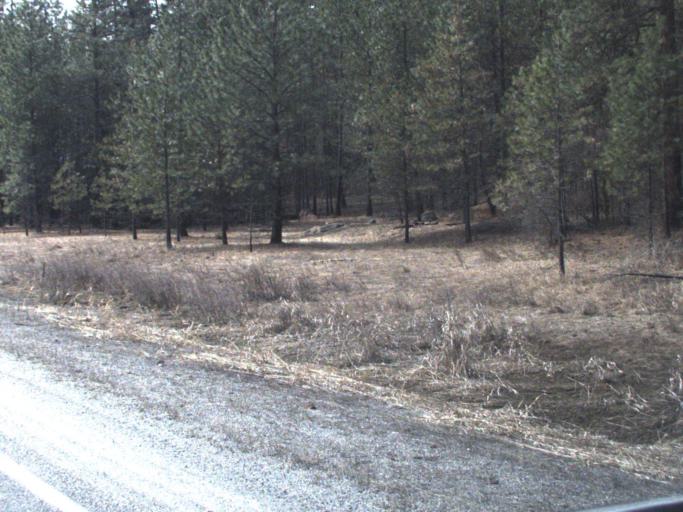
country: US
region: Washington
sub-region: Pend Oreille County
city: Newport
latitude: 48.3958
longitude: -117.3140
